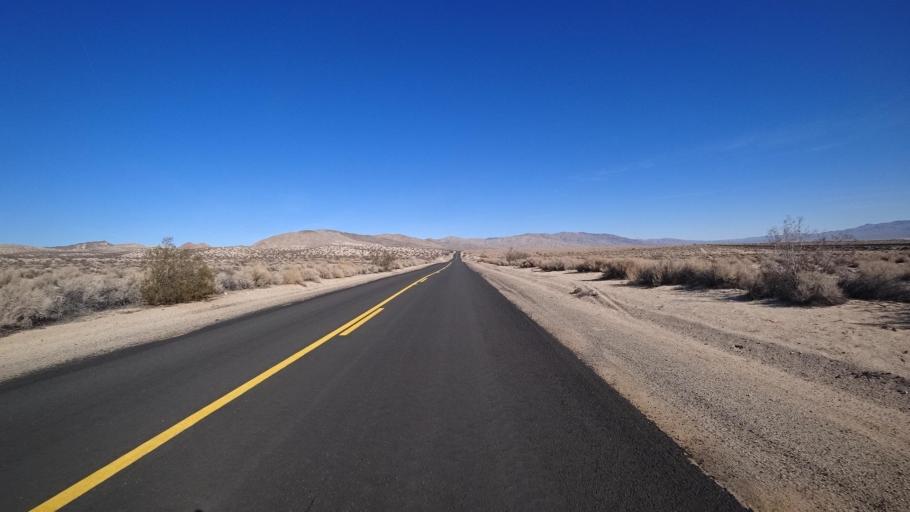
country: US
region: California
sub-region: Kern County
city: California City
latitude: 35.3132
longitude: -117.9644
